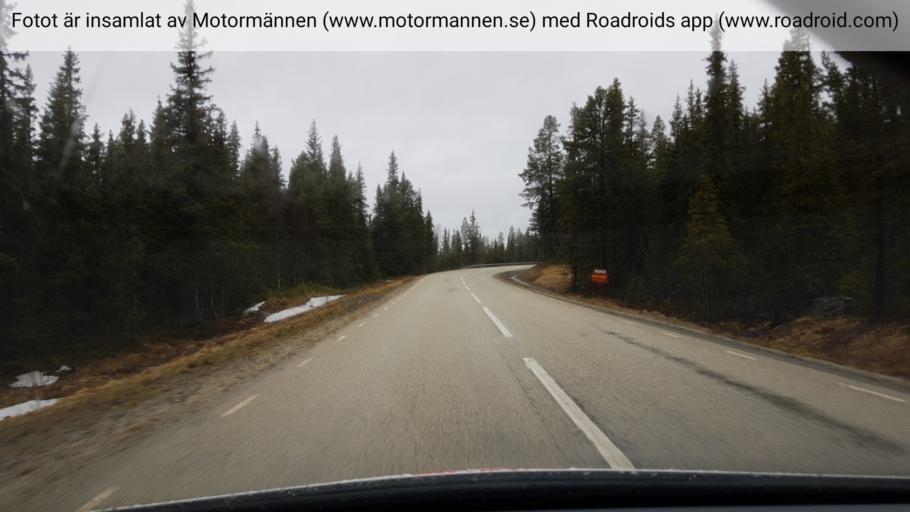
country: SE
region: Jaemtland
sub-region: Are Kommun
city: Are
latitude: 62.8361
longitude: 12.8422
